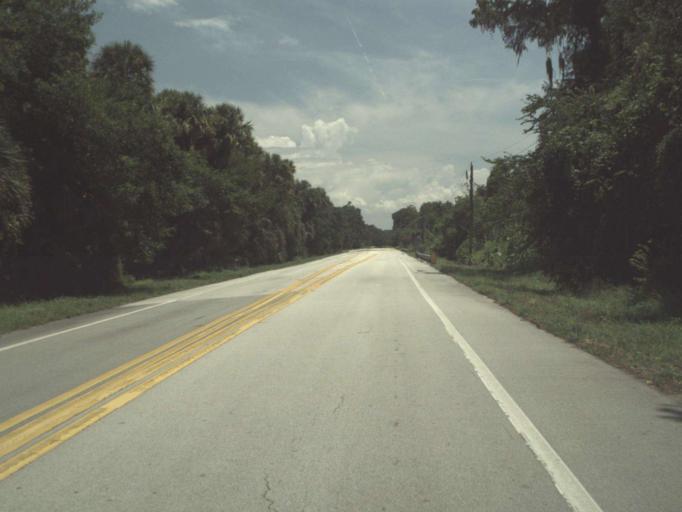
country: US
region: Florida
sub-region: Martin County
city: Indiantown
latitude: 27.0549
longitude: -80.6451
